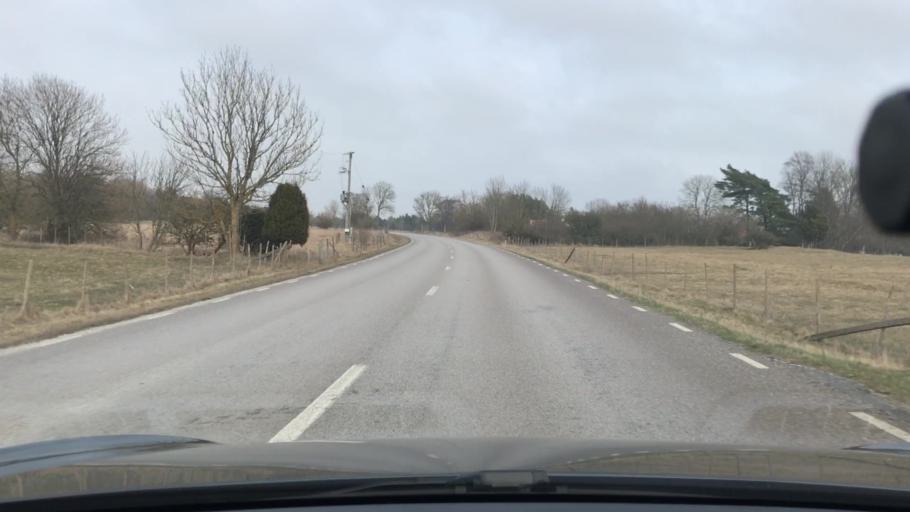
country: SE
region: Gotland
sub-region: Gotland
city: Slite
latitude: 57.4350
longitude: 18.6829
